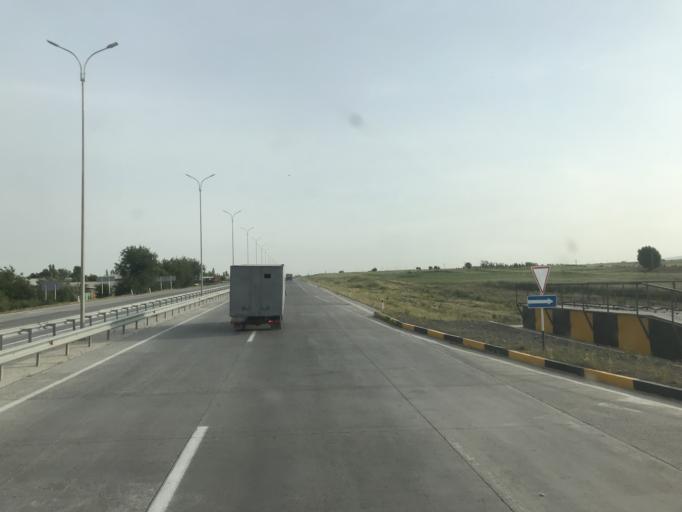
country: UZ
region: Toshkent
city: Qibray
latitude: 41.5562
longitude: 69.4078
